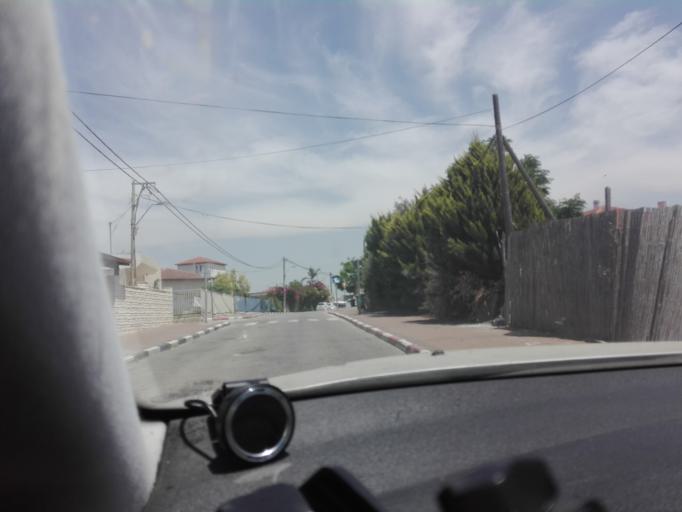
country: IL
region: Central District
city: Bene 'Ayish
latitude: 31.7327
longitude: 34.7487
